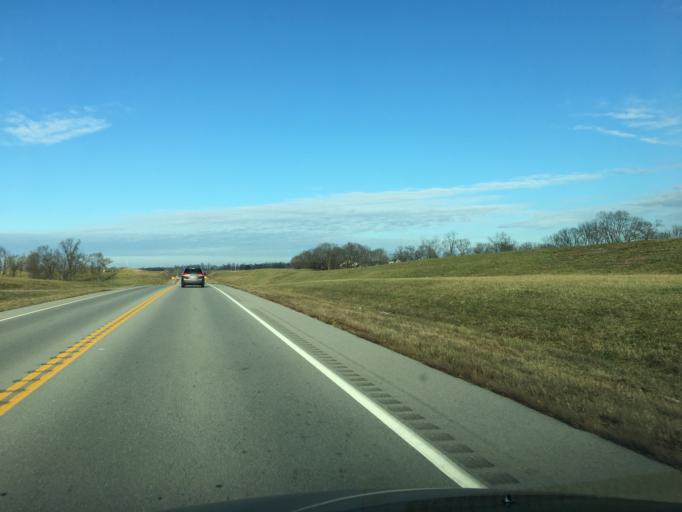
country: US
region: Kentucky
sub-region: Scott County
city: Georgetown
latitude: 38.2371
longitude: -84.5857
